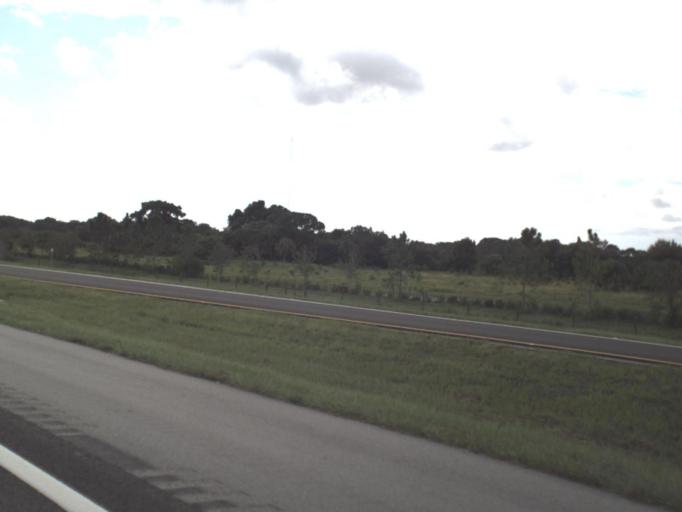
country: US
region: Florida
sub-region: Sarasota County
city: Plantation
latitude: 27.1098
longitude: -82.3808
